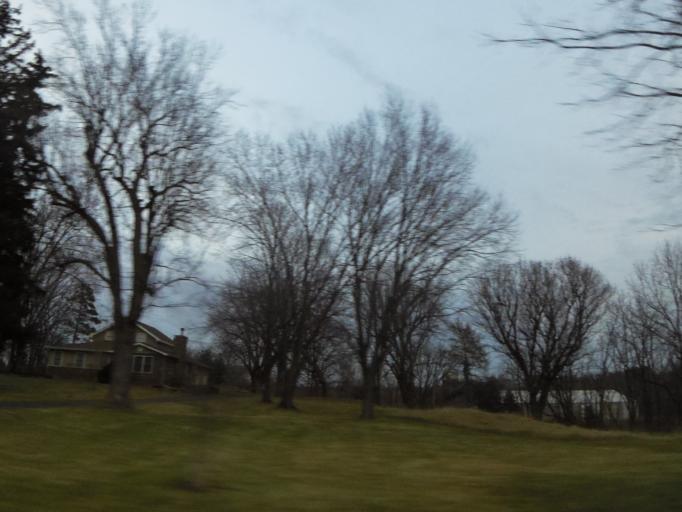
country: US
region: Wisconsin
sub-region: Pierce County
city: River Falls
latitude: 44.8919
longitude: -92.5985
